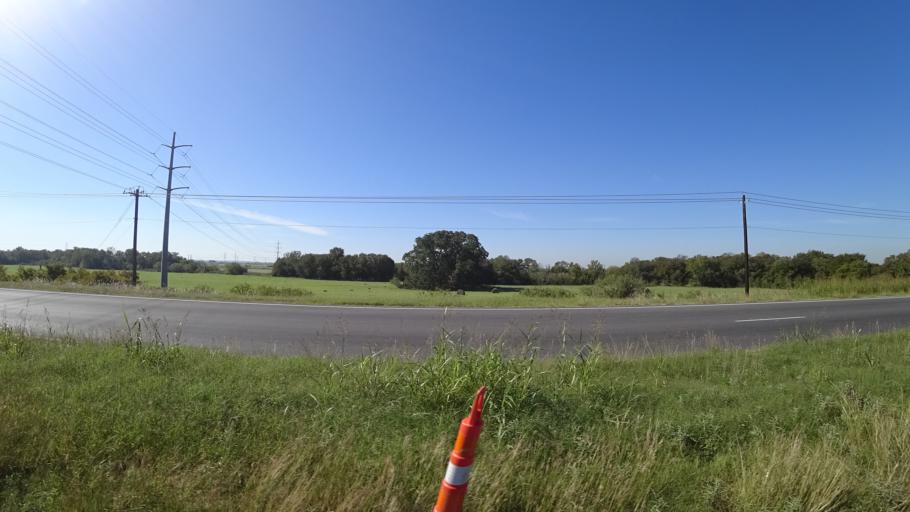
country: US
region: Texas
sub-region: Travis County
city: Hornsby Bend
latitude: 30.2560
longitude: -97.6101
